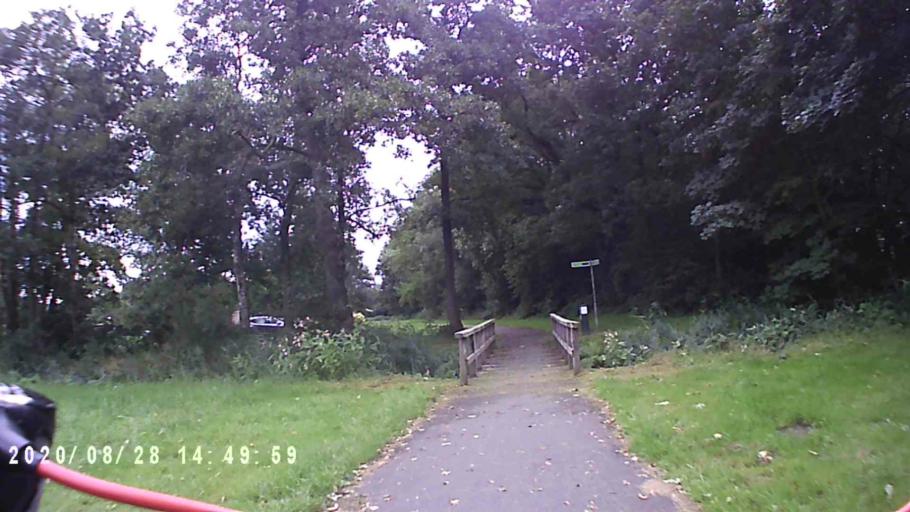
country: NL
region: Groningen
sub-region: Gemeente Groningen
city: Groningen
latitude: 53.1702
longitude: 6.5533
